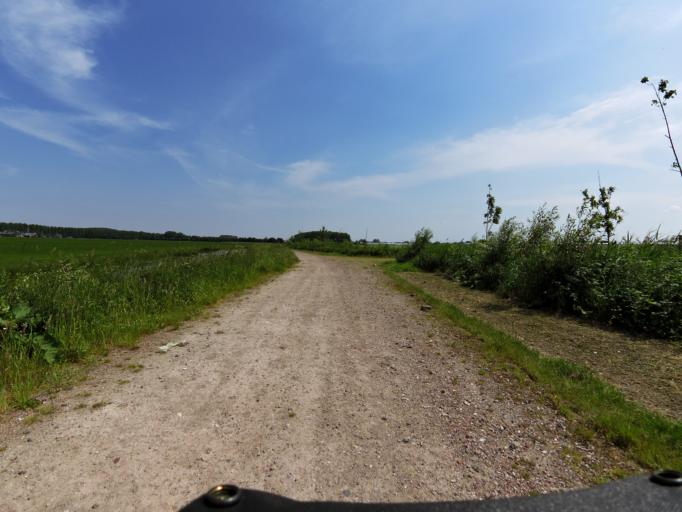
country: NL
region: North Brabant
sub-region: Gemeente Aalburg
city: Aalburg
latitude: 51.7945
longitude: 5.0850
